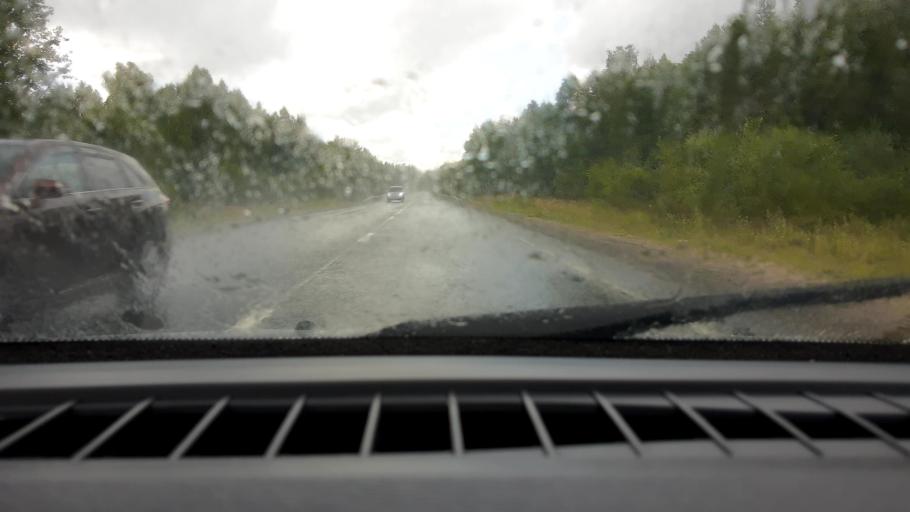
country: RU
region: Nizjnij Novgorod
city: Linda
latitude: 56.6640
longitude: 44.1316
